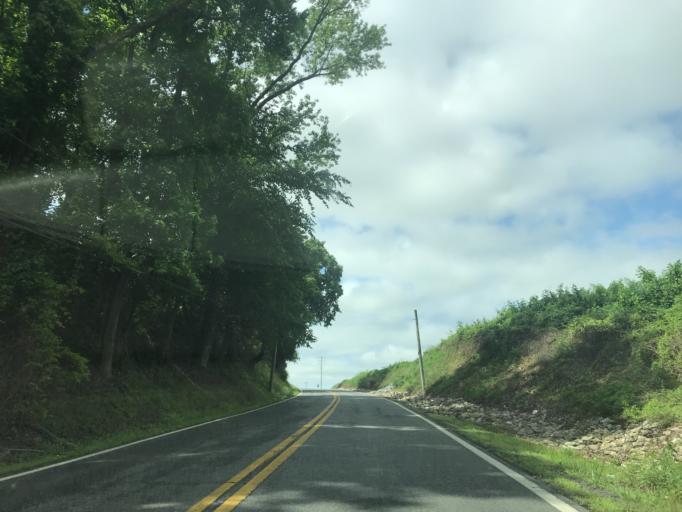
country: US
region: Maryland
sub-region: Caroline County
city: Ridgely
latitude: 38.9153
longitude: -75.9546
